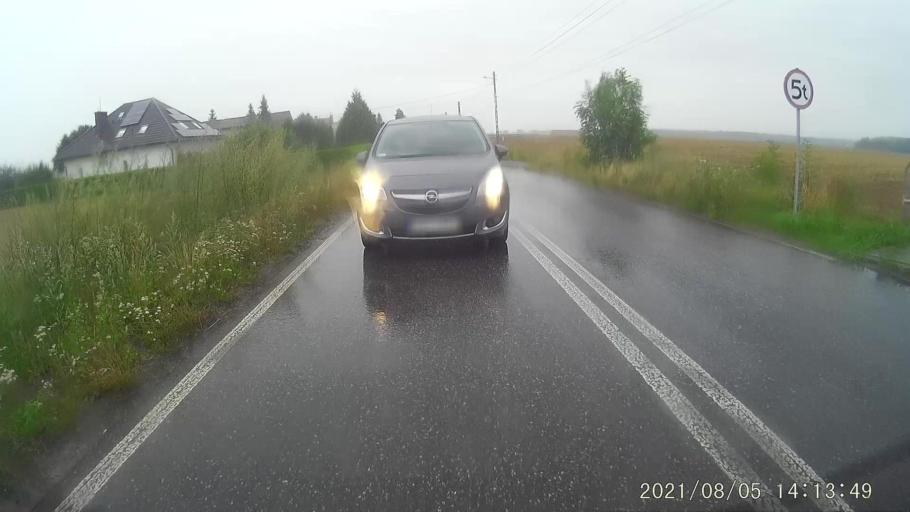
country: PL
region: Opole Voivodeship
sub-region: Powiat krapkowicki
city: Strzeleczki
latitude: 50.4707
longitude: 17.7443
